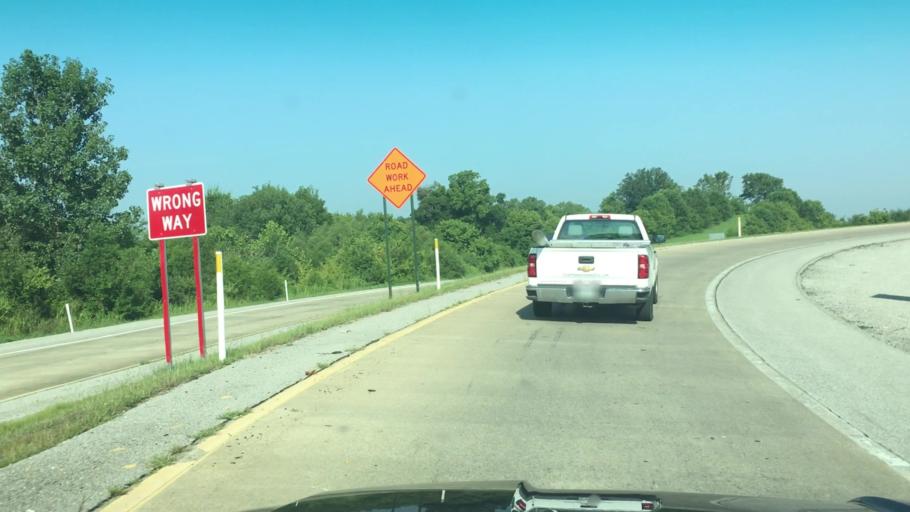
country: US
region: Tennessee
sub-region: Williamson County
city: Thompson's Station
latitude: 35.8201
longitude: -86.8520
